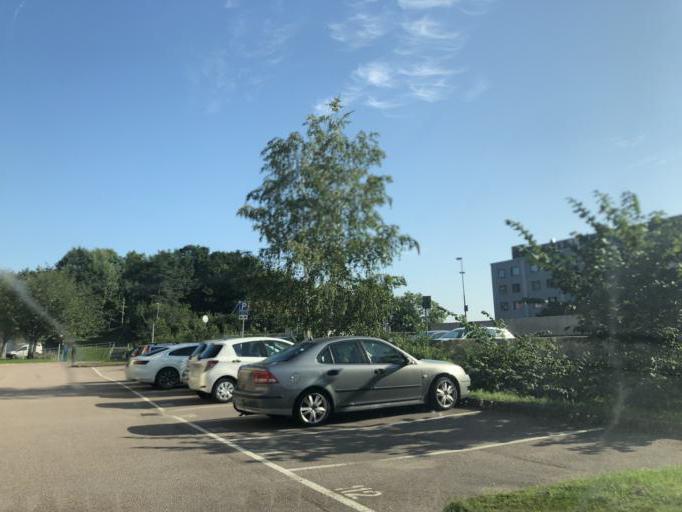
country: SE
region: Vaestra Goetaland
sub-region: Goteborg
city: Goeteborg
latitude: 57.7494
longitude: 11.9876
